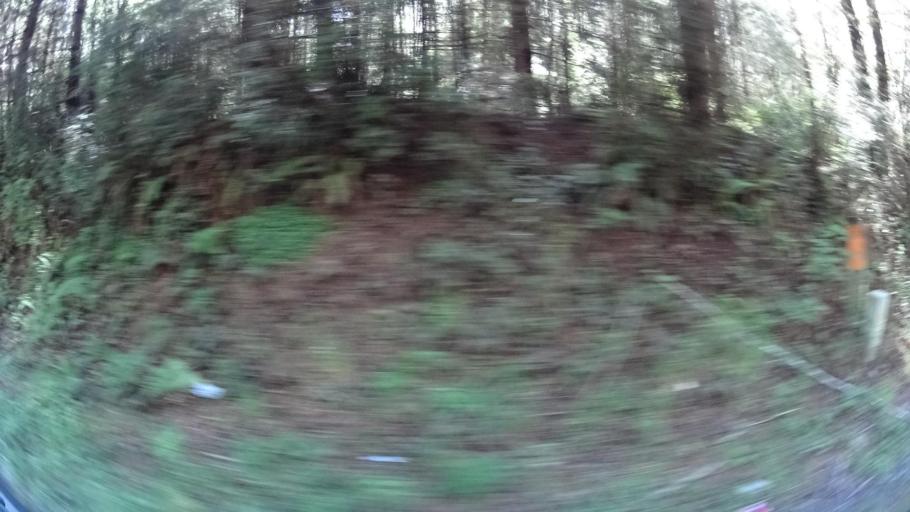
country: US
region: California
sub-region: Humboldt County
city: McKinleyville
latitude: 40.9619
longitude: -124.0716
